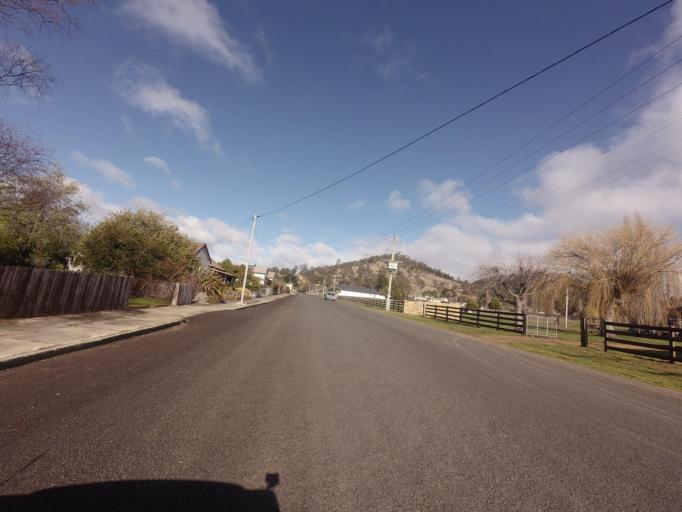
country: AU
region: Tasmania
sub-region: Derwent Valley
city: New Norfolk
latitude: -42.6167
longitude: 146.7158
